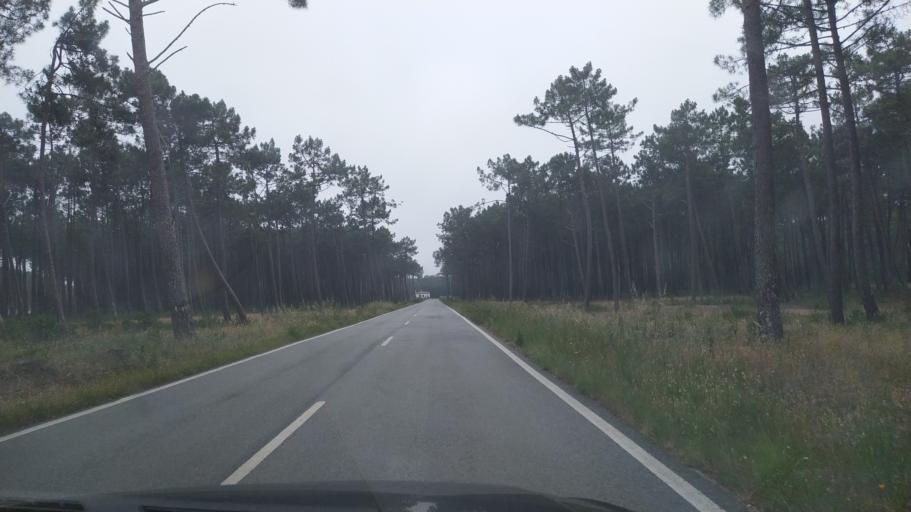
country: PT
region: Aveiro
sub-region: Ilhavo
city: Gafanha da Encarnacao
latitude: 40.5825
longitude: -8.7320
